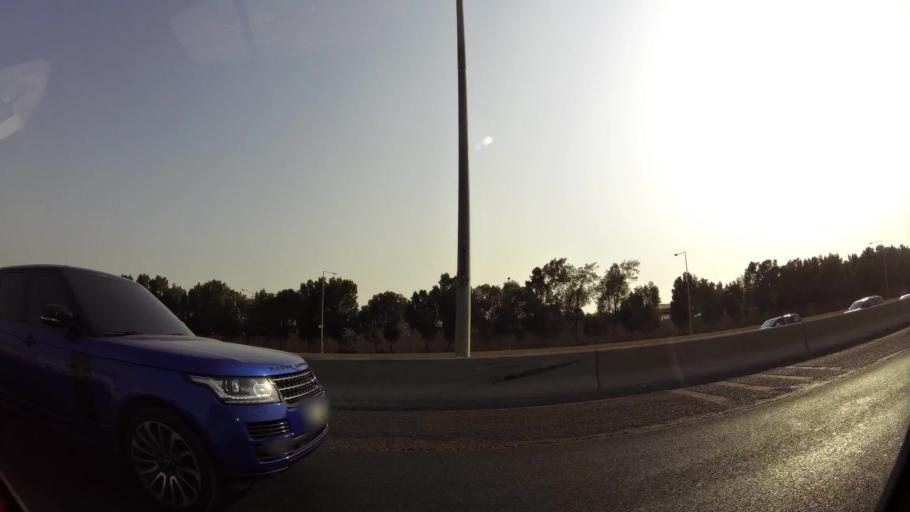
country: KW
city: Al Funaytis
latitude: 29.2424
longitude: 48.0938
